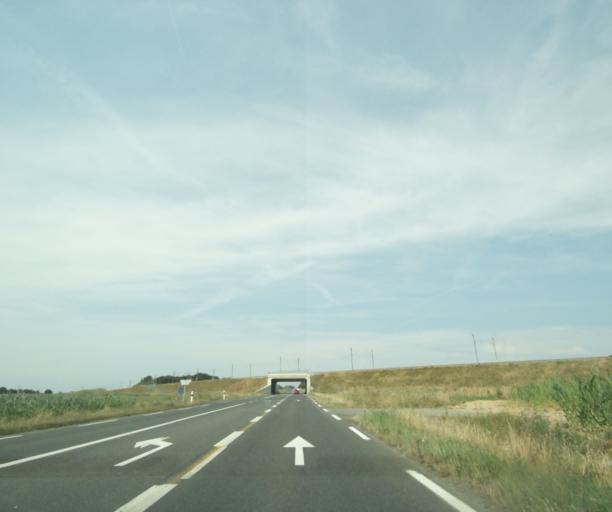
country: FR
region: Centre
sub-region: Departement d'Indre-et-Loire
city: Sorigny
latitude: 47.1788
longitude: 0.6584
